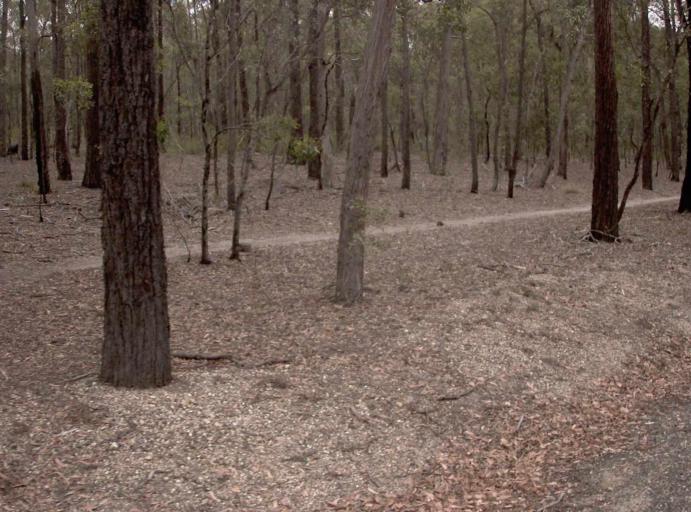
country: AU
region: Victoria
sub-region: Wellington
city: Heyfield
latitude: -37.9456
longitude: 146.7654
